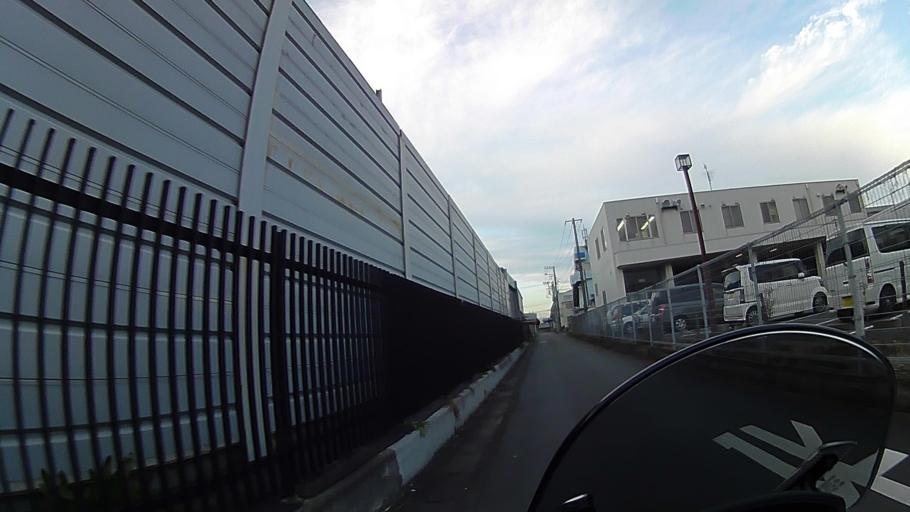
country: JP
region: Kanagawa
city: Minami-rinkan
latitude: 35.4236
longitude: 139.4256
